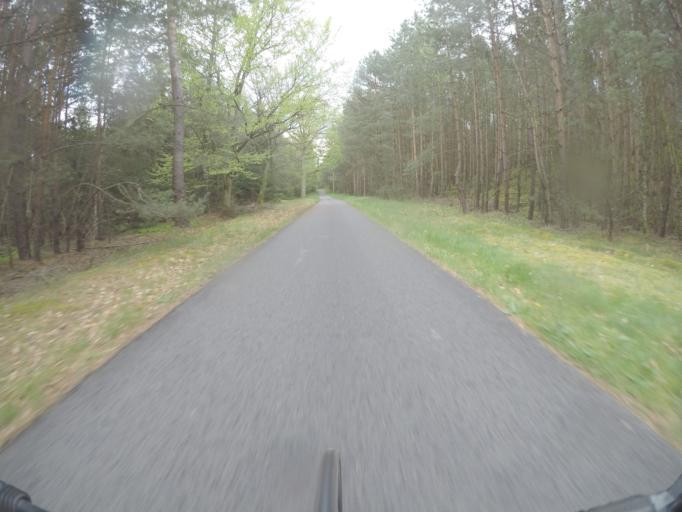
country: DE
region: Brandenburg
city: Biesenthal
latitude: 52.7960
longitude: 13.6266
